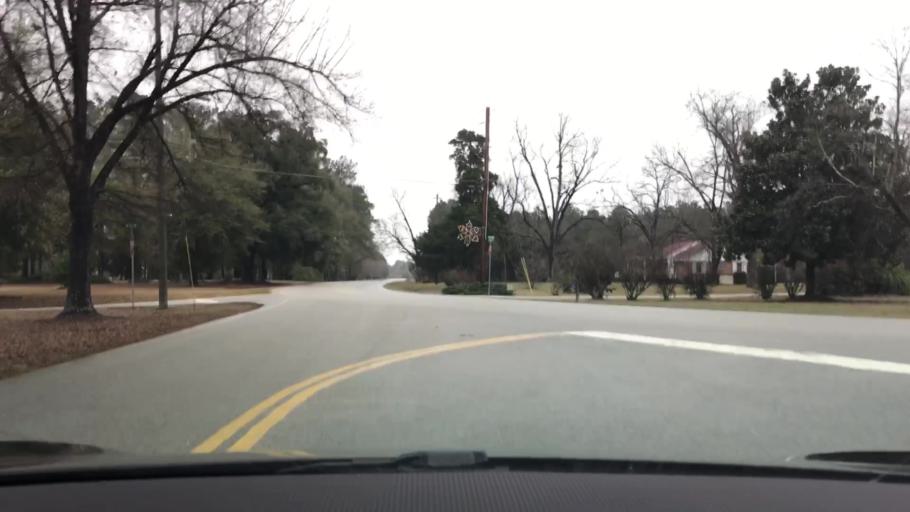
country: US
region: Georgia
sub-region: Jefferson County
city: Wrens
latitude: 33.2166
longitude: -82.4677
